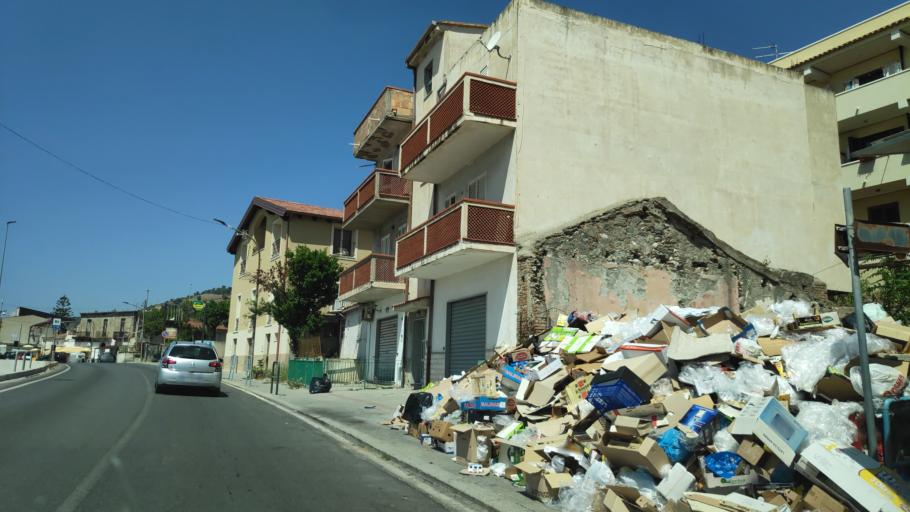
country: IT
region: Calabria
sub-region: Provincia di Reggio Calabria
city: Palizzi Marina
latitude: 37.9190
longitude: 15.9874
